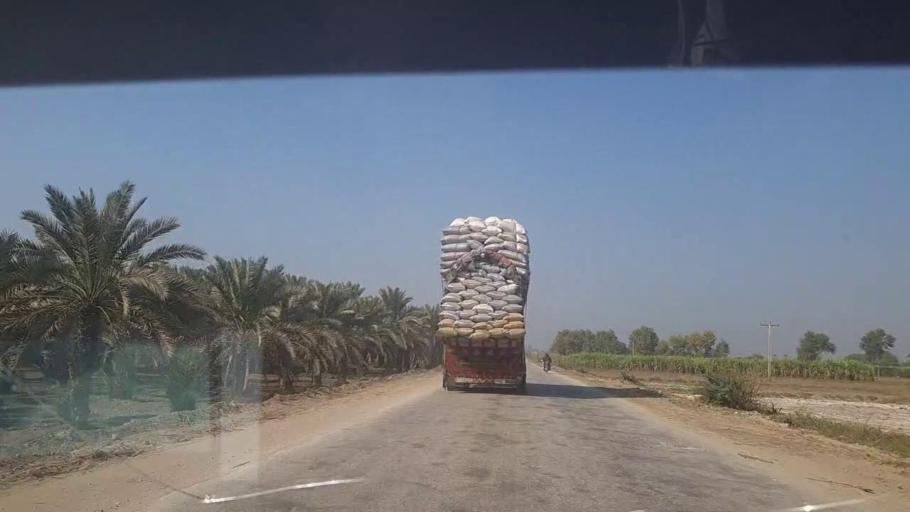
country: PK
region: Sindh
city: Kot Diji
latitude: 27.4208
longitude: 68.6606
